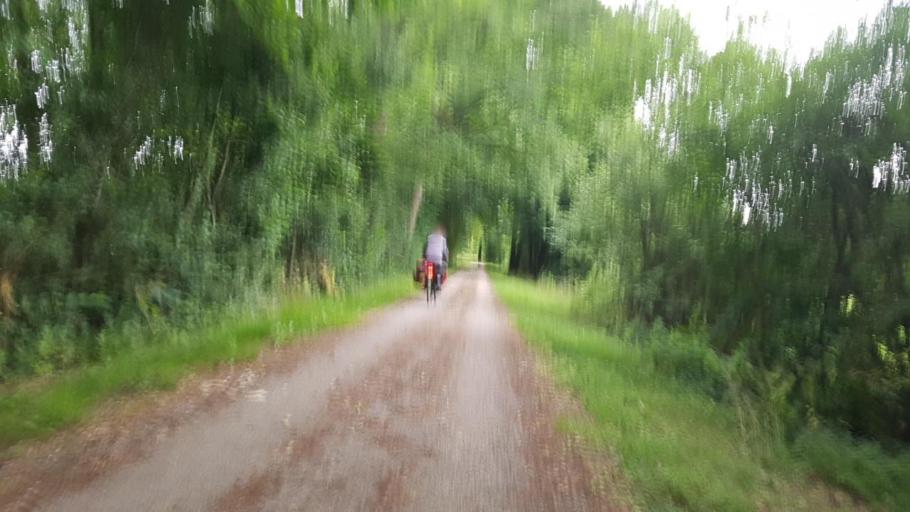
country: FR
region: Picardie
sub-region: Departement de l'Aisne
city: Buironfosse
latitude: 49.9031
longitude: 3.8374
